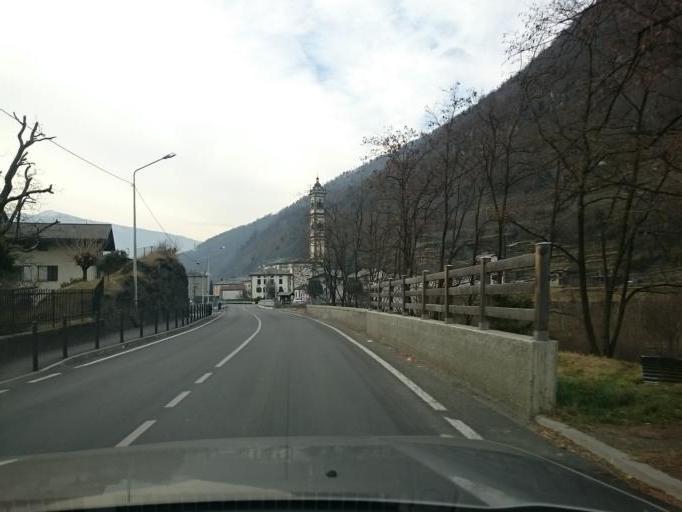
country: IT
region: Lombardy
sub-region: Provincia di Sondrio
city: Grosotto
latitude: 46.2868
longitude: 10.2611
